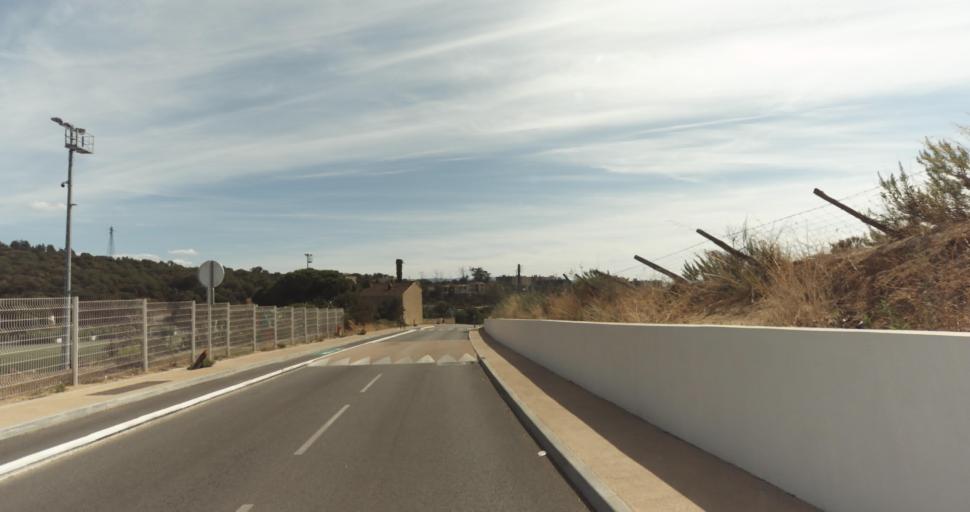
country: FR
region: Corsica
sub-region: Departement de la Corse-du-Sud
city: Ajaccio
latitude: 41.9469
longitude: 8.7582
